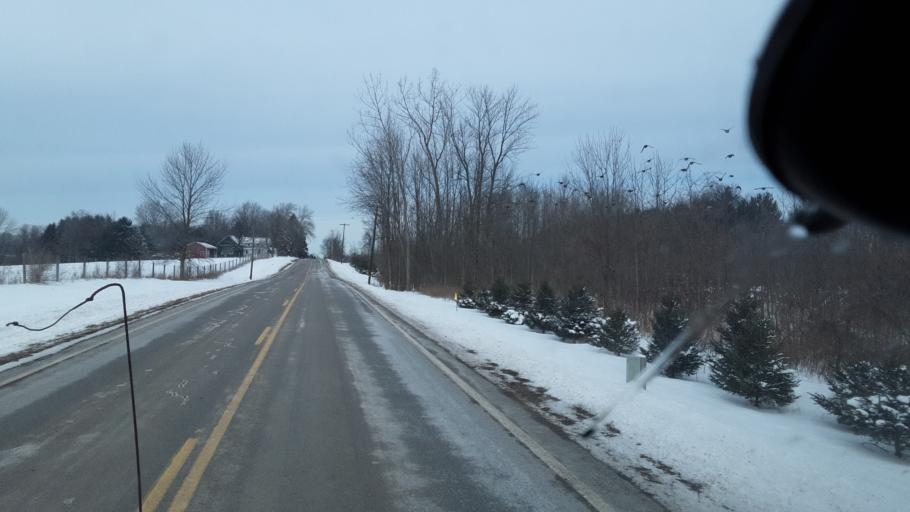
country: US
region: New York
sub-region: Wayne County
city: Lyons
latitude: 43.0941
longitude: -77.0419
